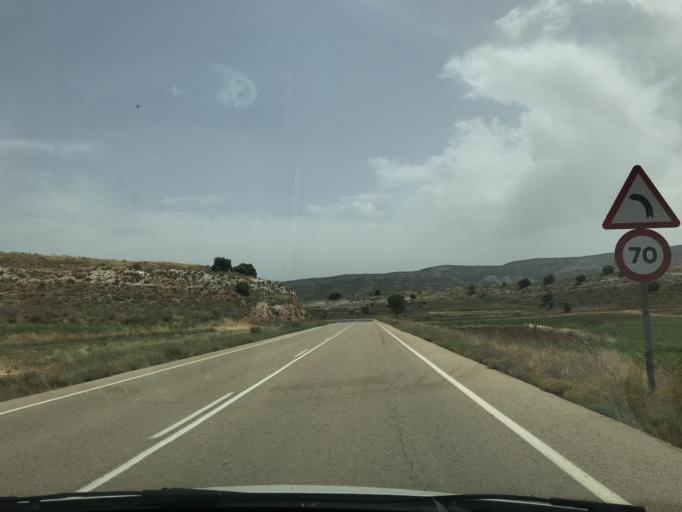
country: ES
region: Castille-La Mancha
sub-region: Provincia de Cuenca
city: Torralba
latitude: 40.2745
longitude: -2.2961
